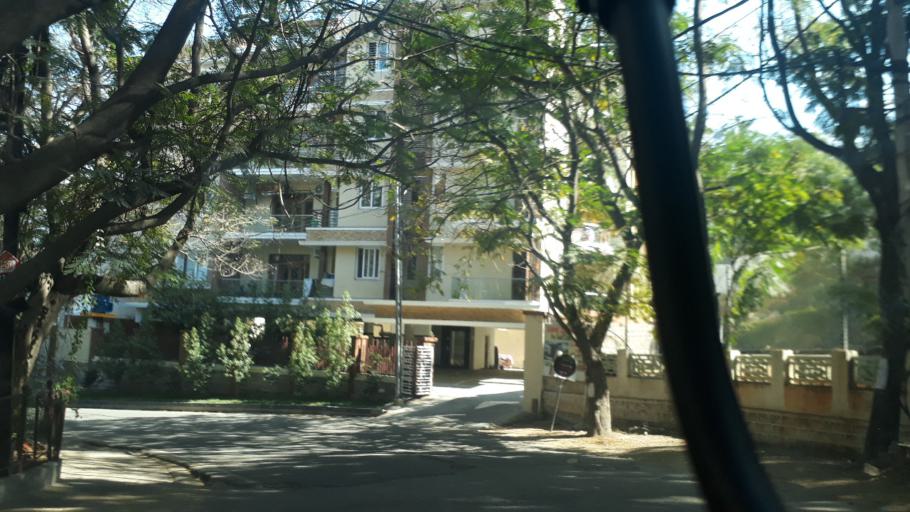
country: IN
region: Telangana
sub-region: Rangareddi
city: Kukatpalli
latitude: 17.4218
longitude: 78.4022
